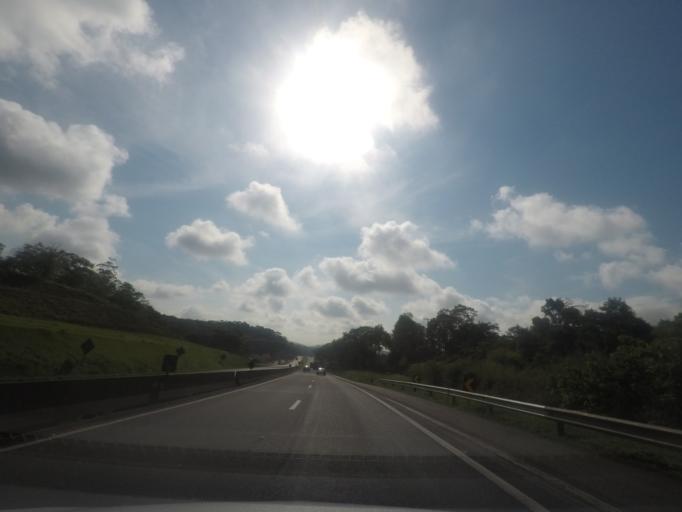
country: BR
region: Parana
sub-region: Antonina
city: Antonina
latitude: -25.5606
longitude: -48.8080
